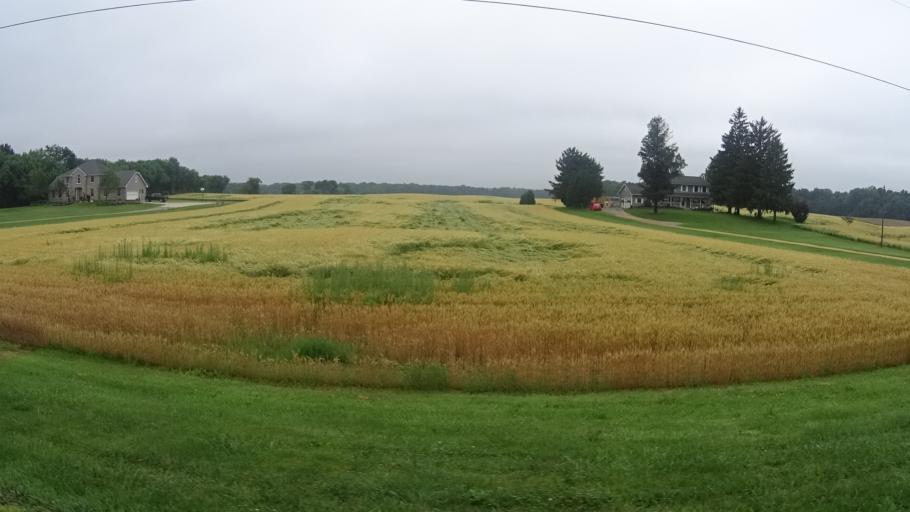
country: US
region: Ohio
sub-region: Erie County
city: Huron
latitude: 41.3503
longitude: -82.5763
